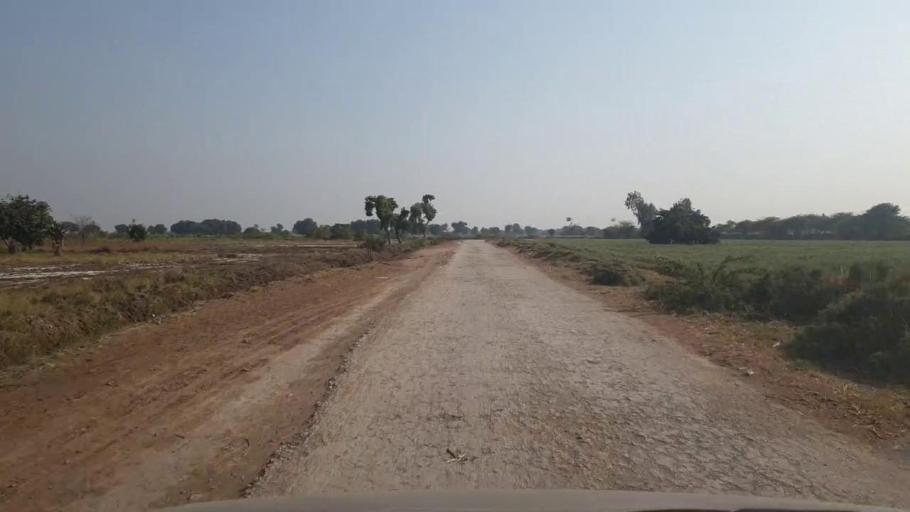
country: PK
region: Sindh
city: Digri
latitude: 25.2538
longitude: 69.1826
